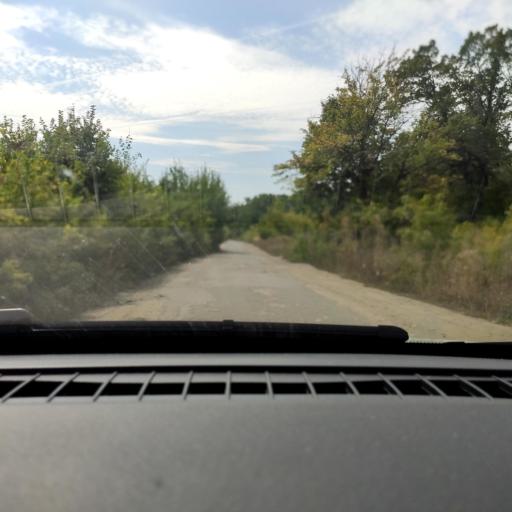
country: RU
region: Voronezj
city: Pridonskoy
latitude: 51.7480
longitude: 39.0751
